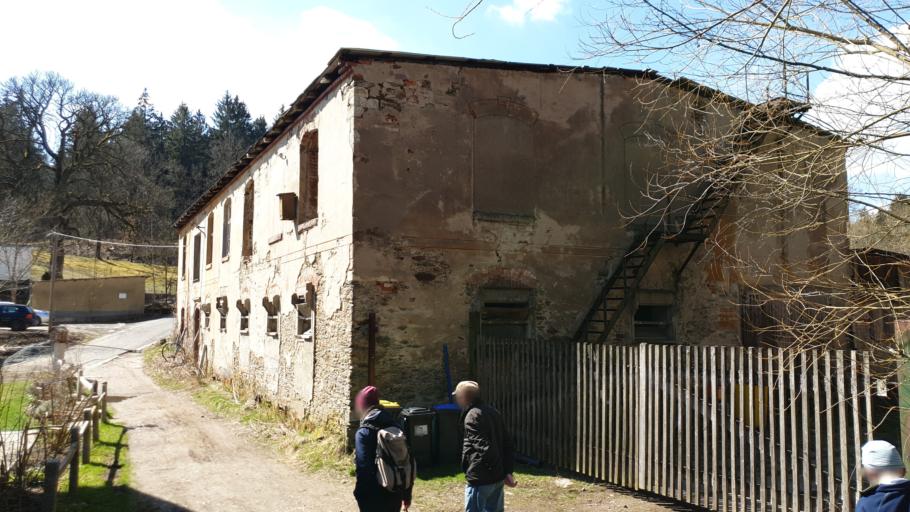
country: DE
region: Saxony
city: Gelenau
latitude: 50.7457
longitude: 12.9710
